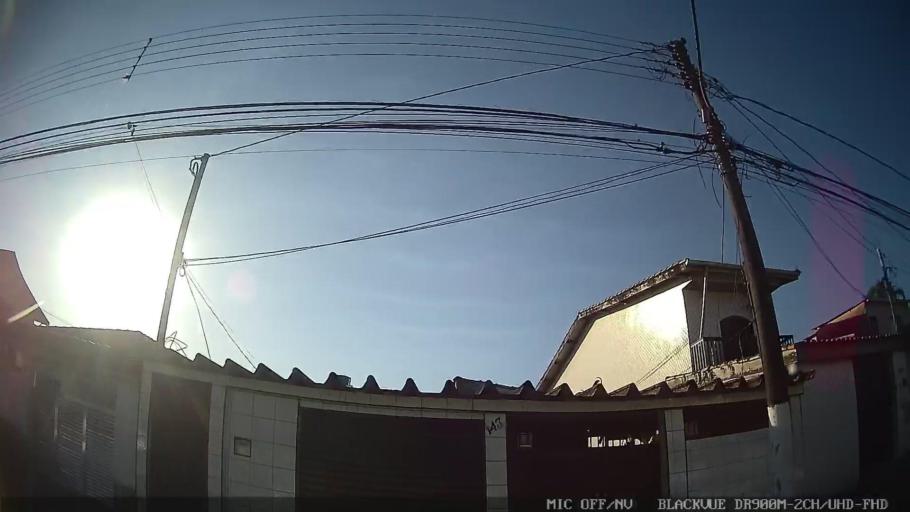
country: BR
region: Sao Paulo
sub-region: Guaruja
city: Guaruja
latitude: -23.9662
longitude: -46.2799
